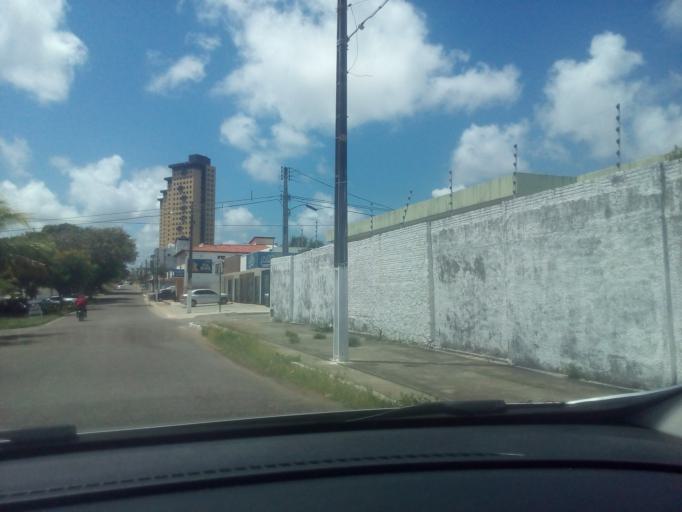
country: BR
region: Rio Grande do Norte
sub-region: Parnamirim
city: Parnamirim
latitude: -5.8673
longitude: -35.2105
